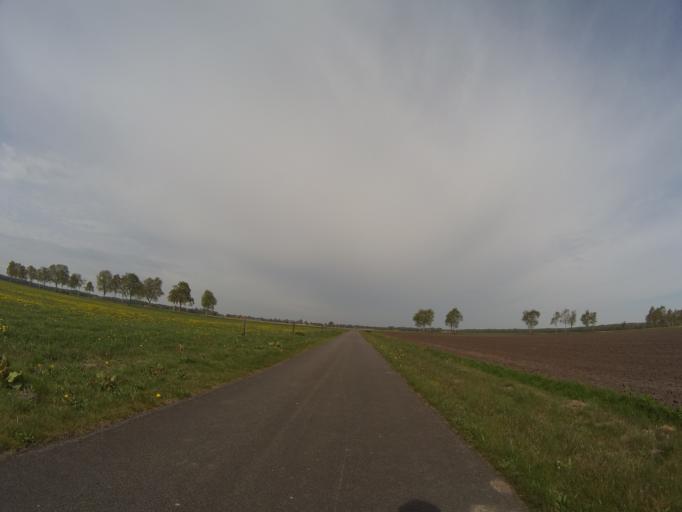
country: NL
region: Drenthe
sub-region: Gemeente Coevorden
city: Sleen
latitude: 52.8263
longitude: 6.6857
